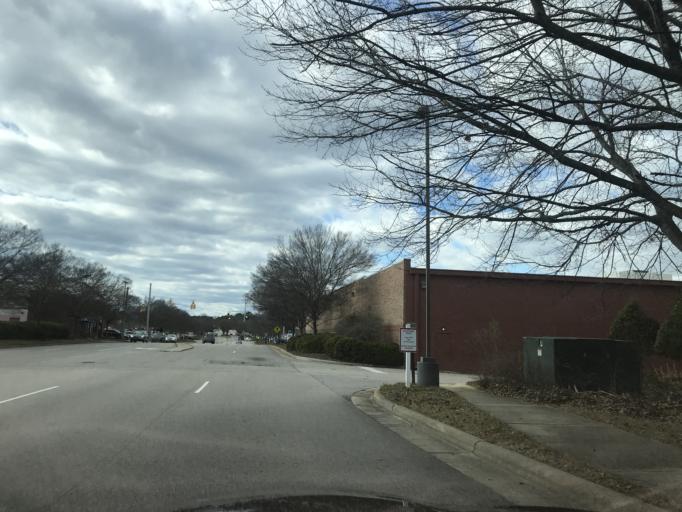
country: US
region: North Carolina
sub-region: Wake County
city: Cary
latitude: 35.7602
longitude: -78.7349
